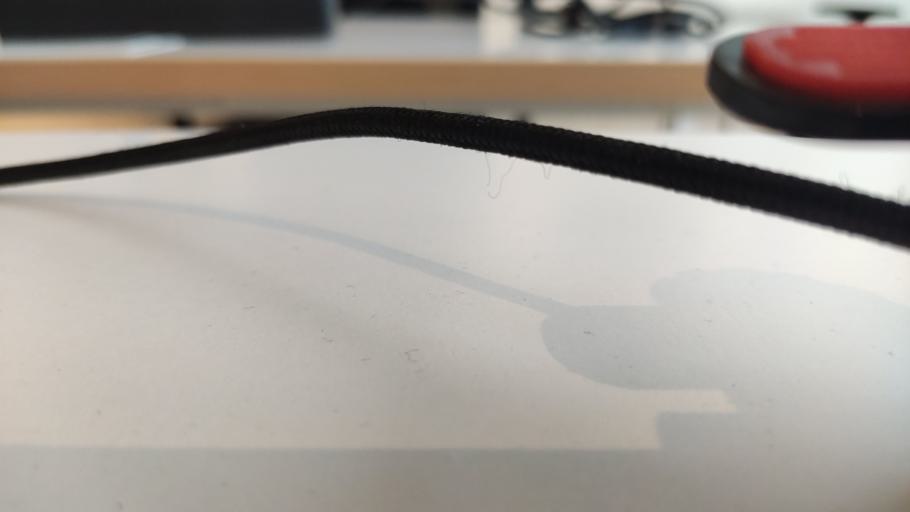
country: RU
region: Moskovskaya
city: Klin
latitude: 56.3635
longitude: 36.7642
